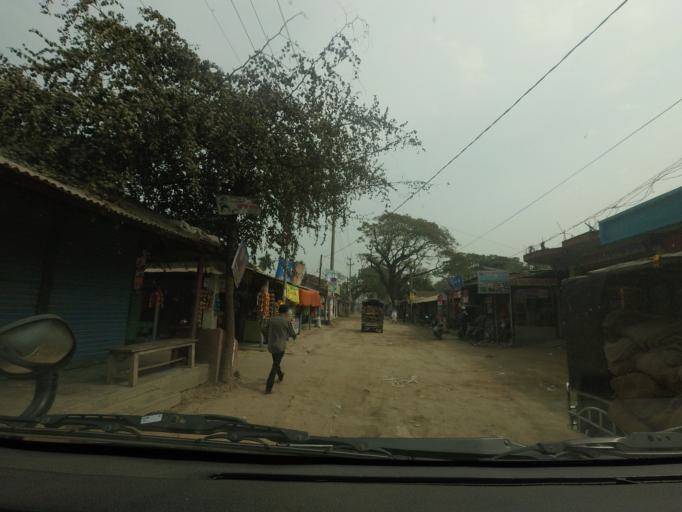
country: BD
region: Dhaka
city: Kishorganj
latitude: 24.3399
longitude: 90.7971
